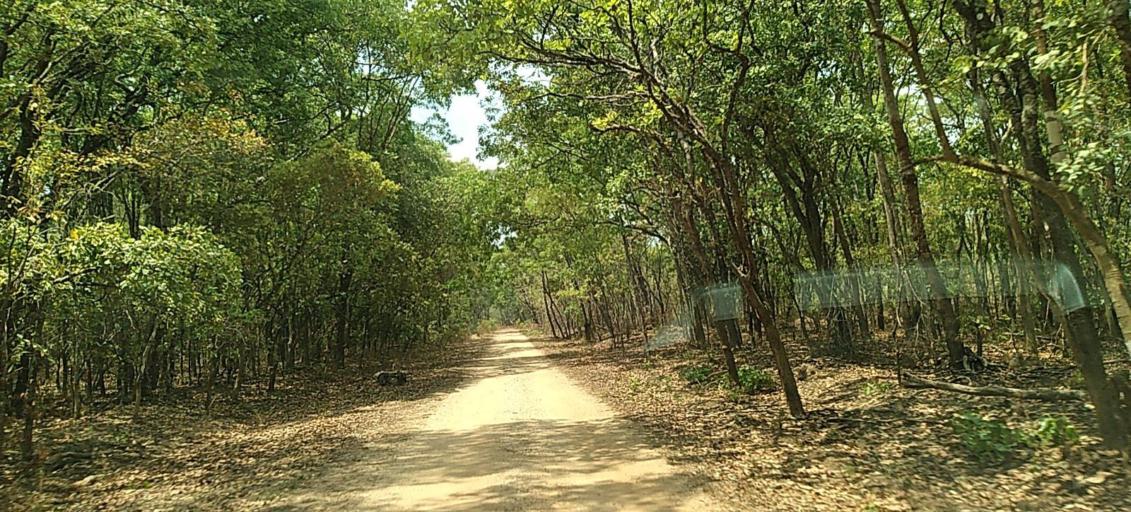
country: ZM
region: Copperbelt
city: Chingola
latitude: -12.7670
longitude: 27.7059
